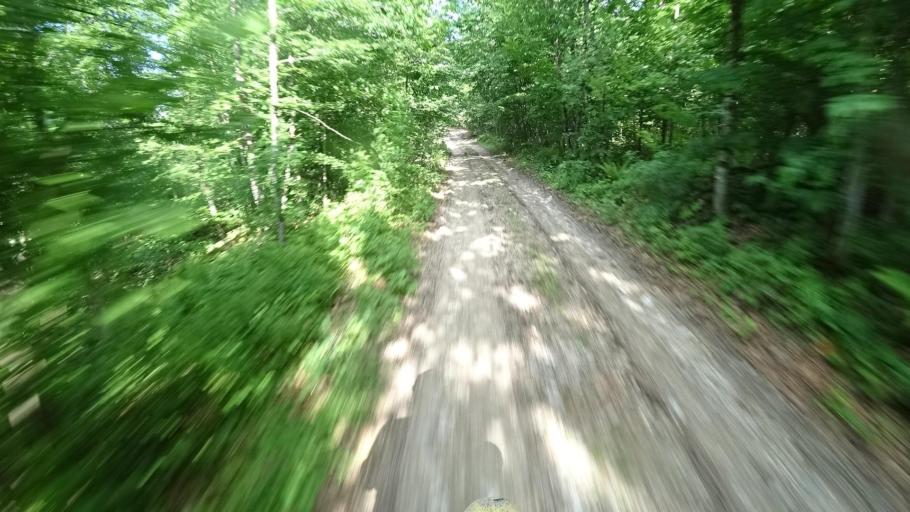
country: BA
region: Federation of Bosnia and Herzegovina
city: Bosanska Krupa
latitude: 44.7636
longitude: 16.2779
